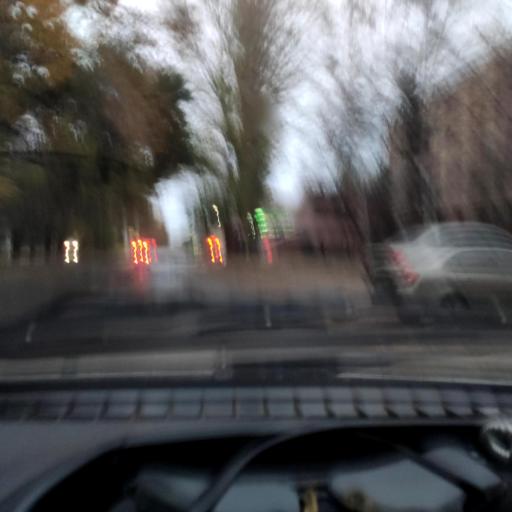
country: RU
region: Samara
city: Tol'yatti
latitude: 53.5192
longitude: 49.4294
